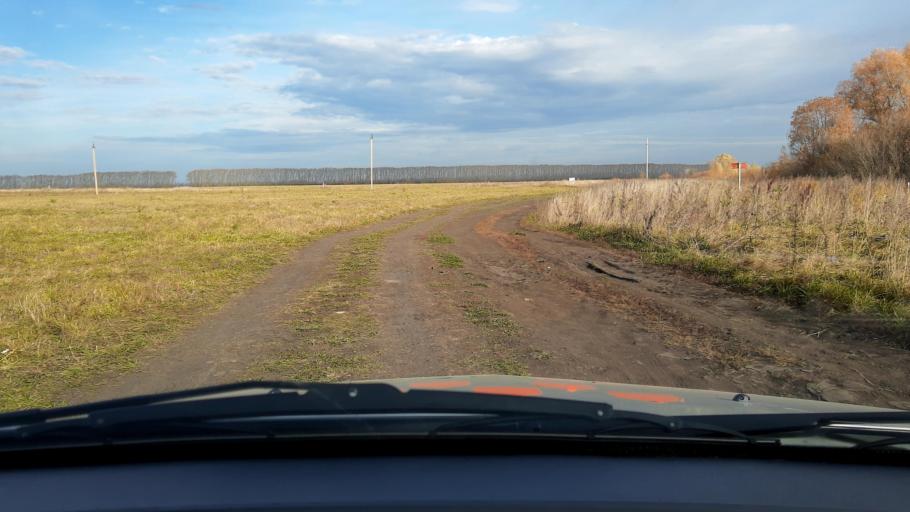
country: RU
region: Bashkortostan
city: Asanovo
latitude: 54.8081
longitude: 55.6114
